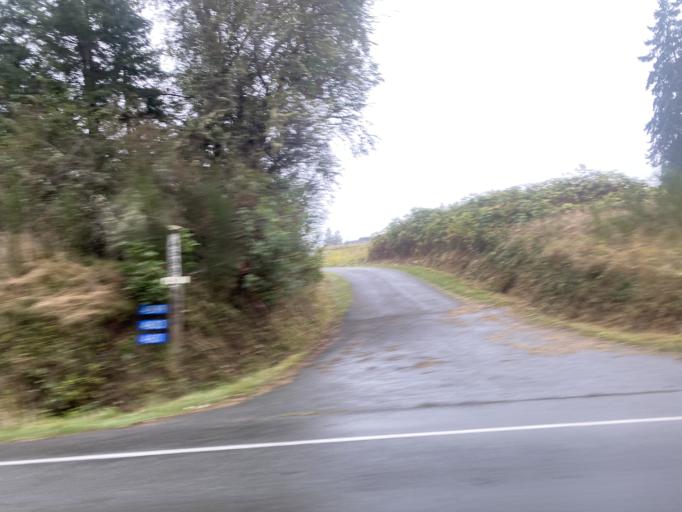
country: US
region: Washington
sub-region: Island County
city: Freeland
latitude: 48.0442
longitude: -122.5069
